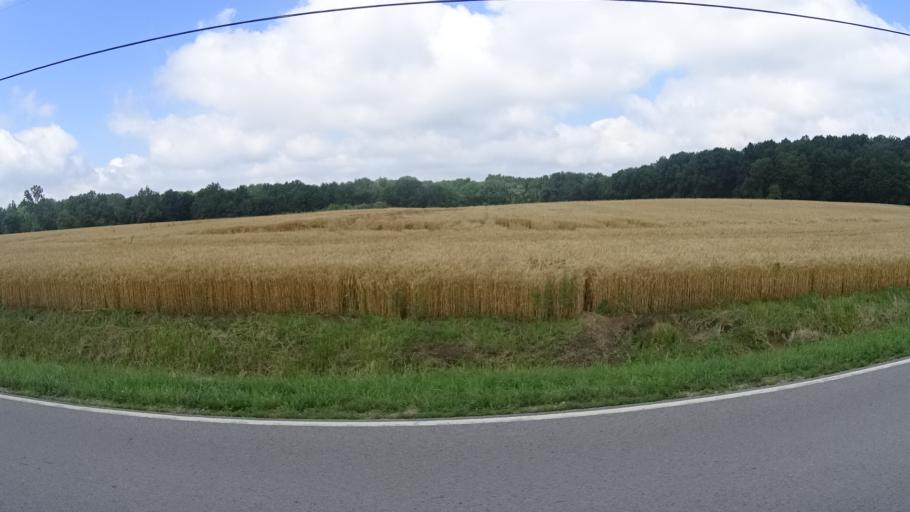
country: US
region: Ohio
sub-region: Huron County
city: Wakeman
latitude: 41.3159
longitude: -82.4136
